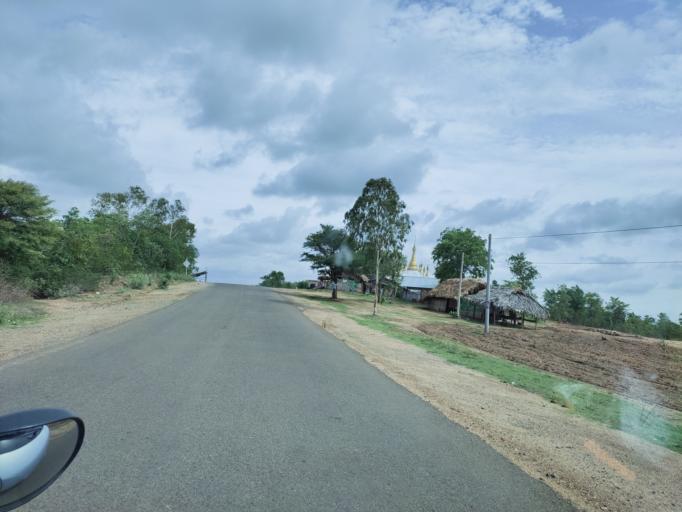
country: MM
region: Magway
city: Chauk
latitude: 20.9697
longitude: 95.0567
